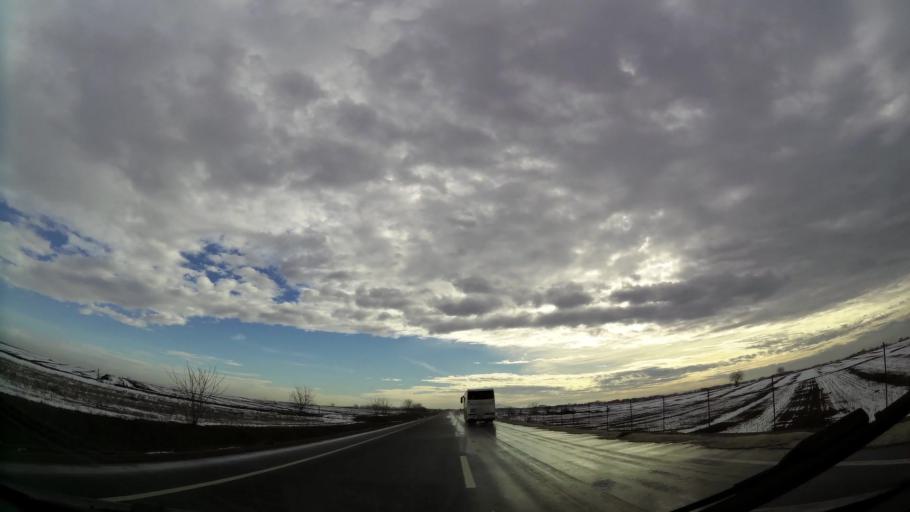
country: RS
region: Central Serbia
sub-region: Belgrade
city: Surcin
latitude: 44.8083
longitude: 20.3019
